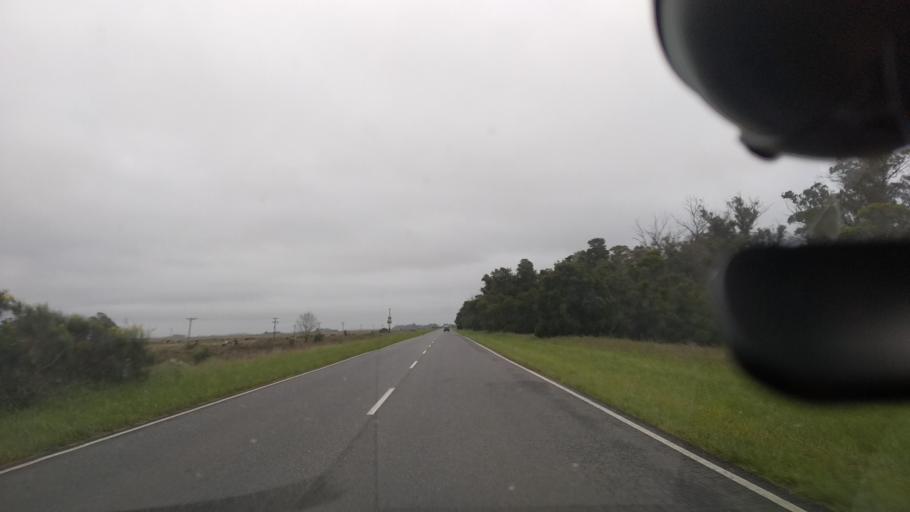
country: AR
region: Buenos Aires
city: Veronica
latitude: -35.4534
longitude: -57.3339
